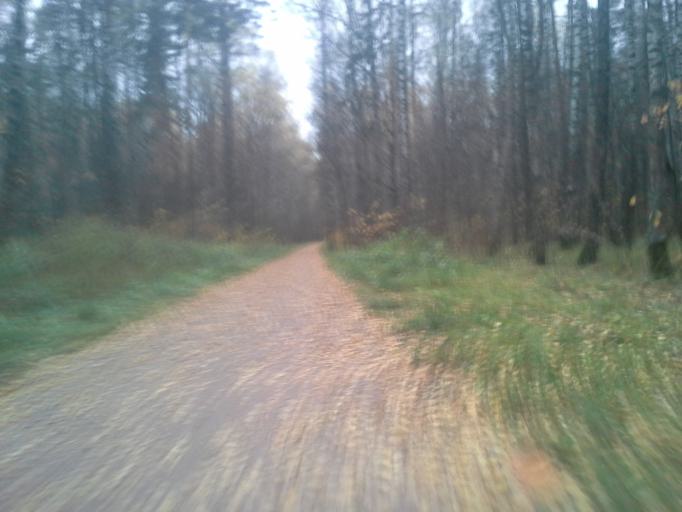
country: RU
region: Moskovskaya
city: Zarech'ye
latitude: 55.6667
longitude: 37.3923
